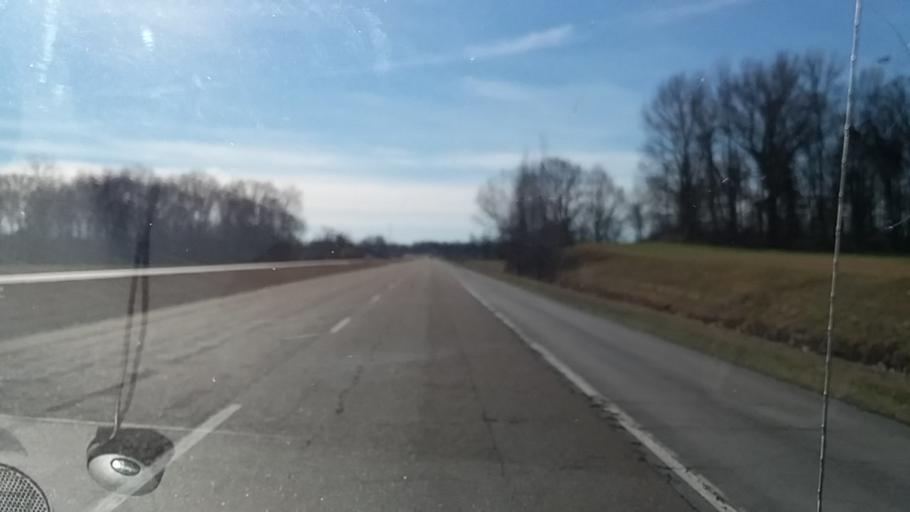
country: US
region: Tennessee
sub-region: Lauderdale County
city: Halls
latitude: 35.9264
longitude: -89.2824
